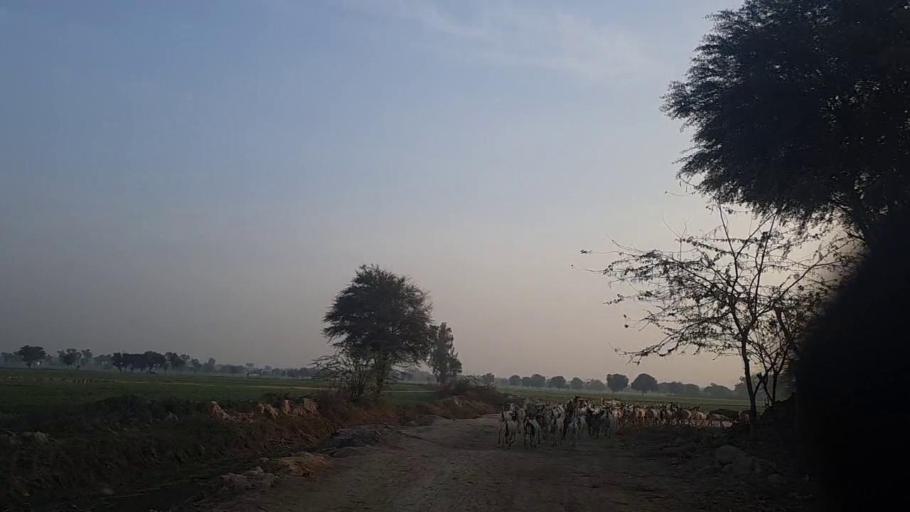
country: PK
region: Sindh
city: Sakrand
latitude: 26.1167
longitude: 68.2326
